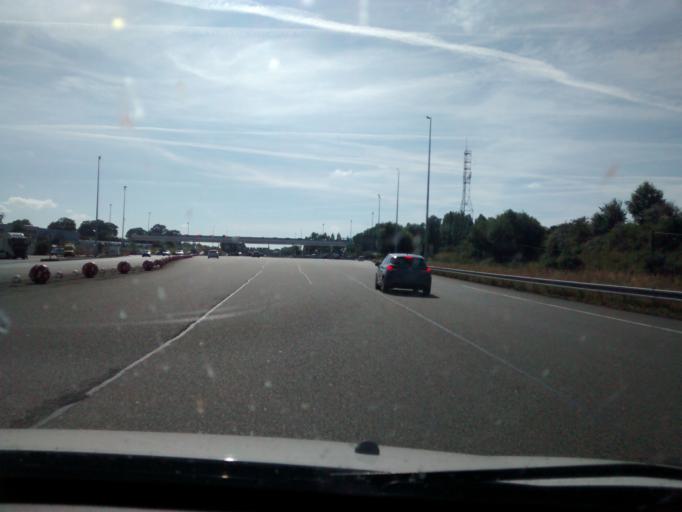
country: FR
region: Pays de la Loire
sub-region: Departement de la Mayenne
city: Saint-Pierre-la-Cour
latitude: 48.0831
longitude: -1.0239
